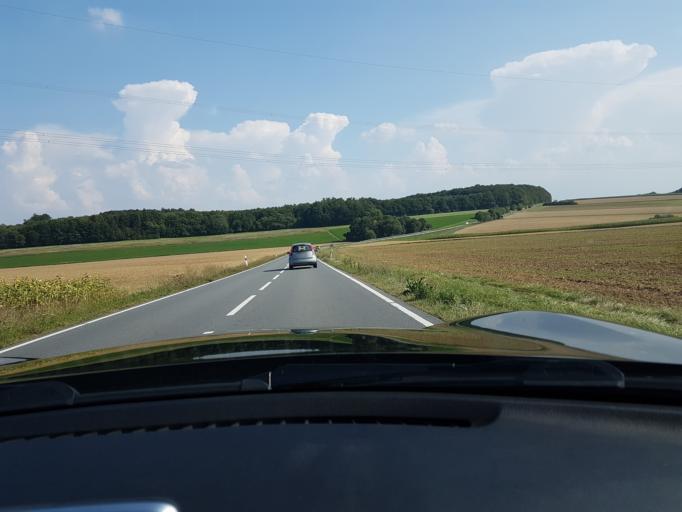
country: DE
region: Baden-Wuerttemberg
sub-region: Karlsruhe Region
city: Buchen
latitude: 49.4976
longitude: 9.3537
